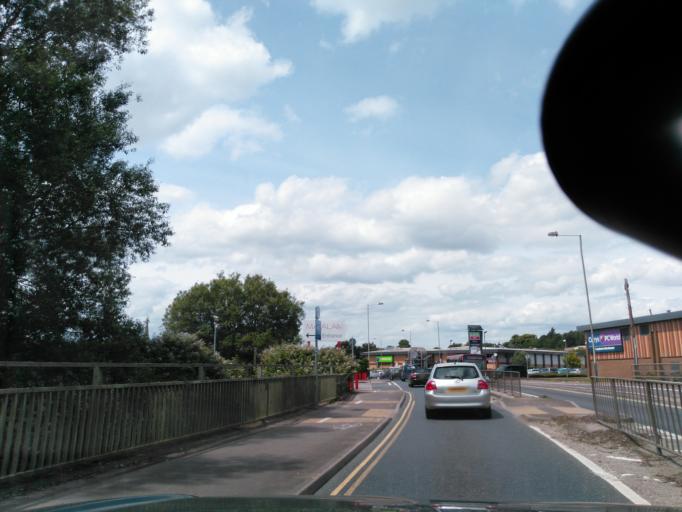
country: GB
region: England
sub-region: Wiltshire
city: Salisbury
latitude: 51.0624
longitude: -1.7795
